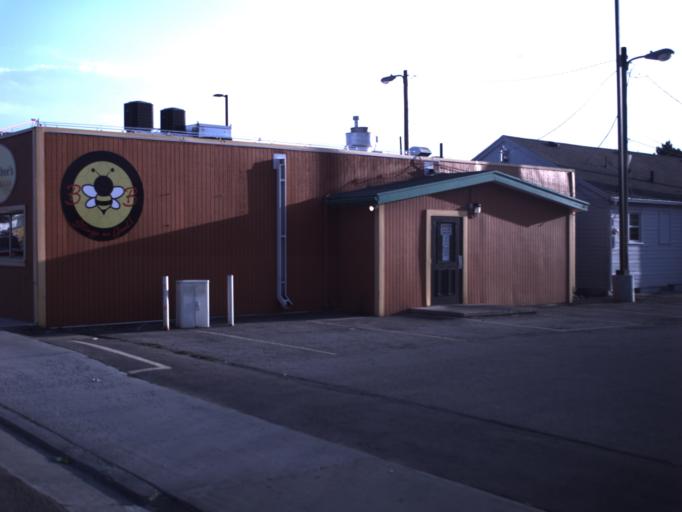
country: US
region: Utah
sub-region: Salt Lake County
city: Midvale
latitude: 40.6068
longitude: -111.8909
